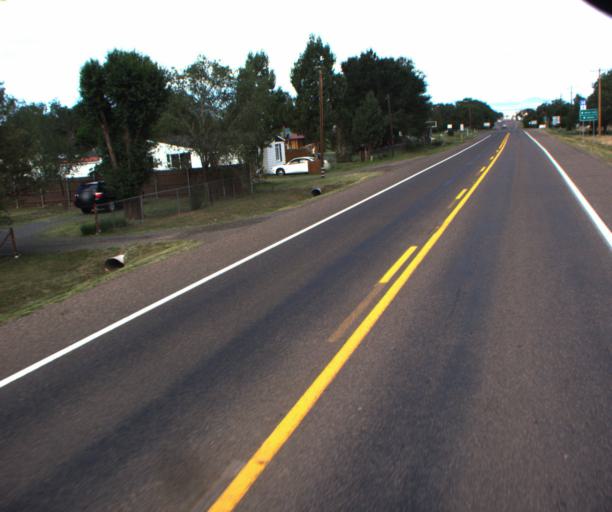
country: US
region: Arizona
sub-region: Apache County
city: Springerville
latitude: 34.1328
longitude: -109.2681
